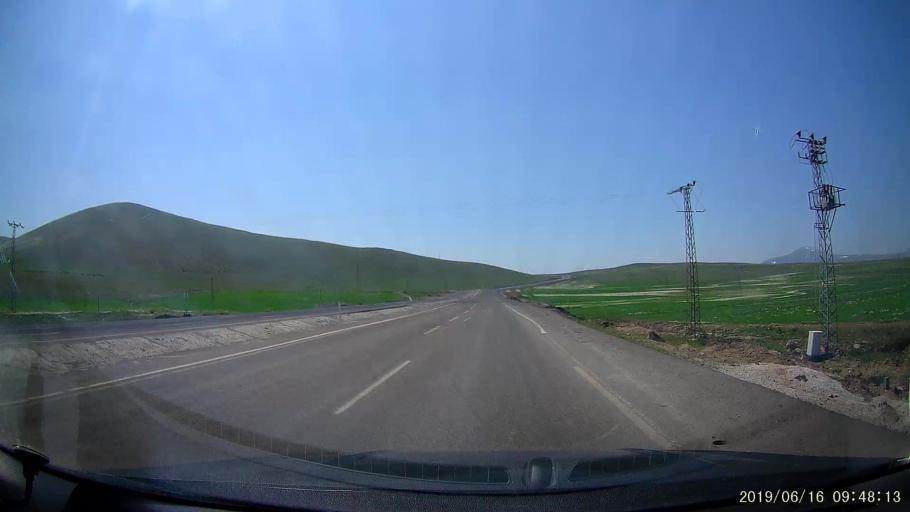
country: TR
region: Kars
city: Digor
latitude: 40.4359
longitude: 43.3512
